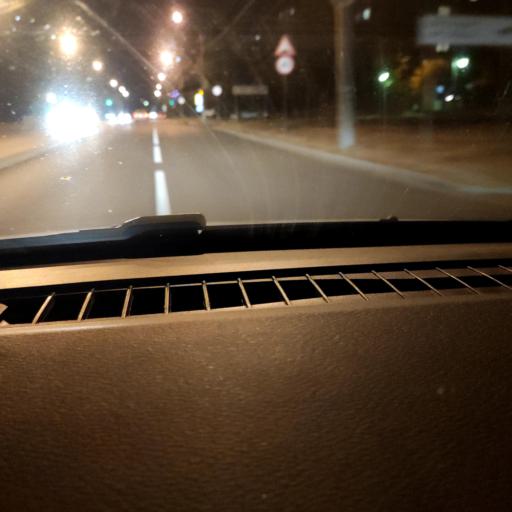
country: RU
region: Voronezj
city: Podgornoye
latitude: 51.7167
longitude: 39.1655
